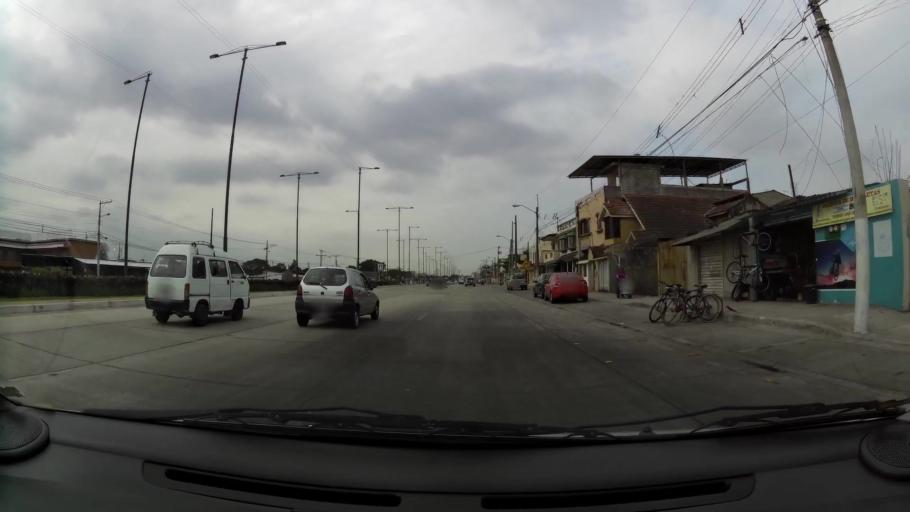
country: EC
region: Guayas
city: Eloy Alfaro
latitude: -2.1182
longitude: -79.8998
